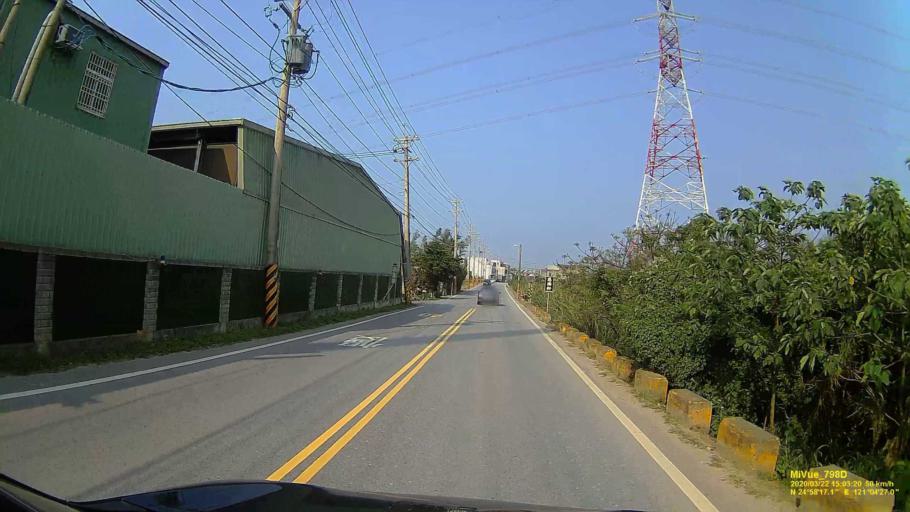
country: TW
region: Taiwan
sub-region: Hsinchu
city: Zhubei
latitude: 24.9717
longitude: 121.0744
